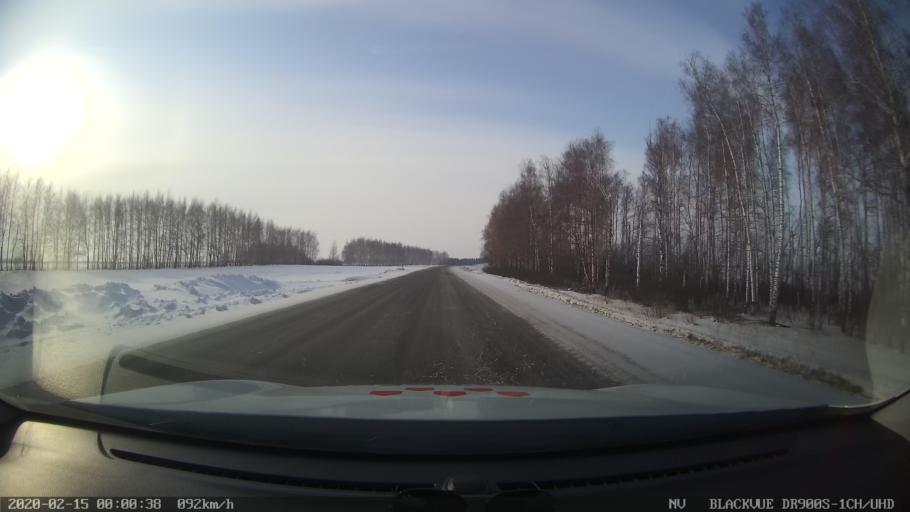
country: RU
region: Tatarstan
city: Kuybyshevskiy Zaton
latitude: 55.3438
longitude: 49.0342
